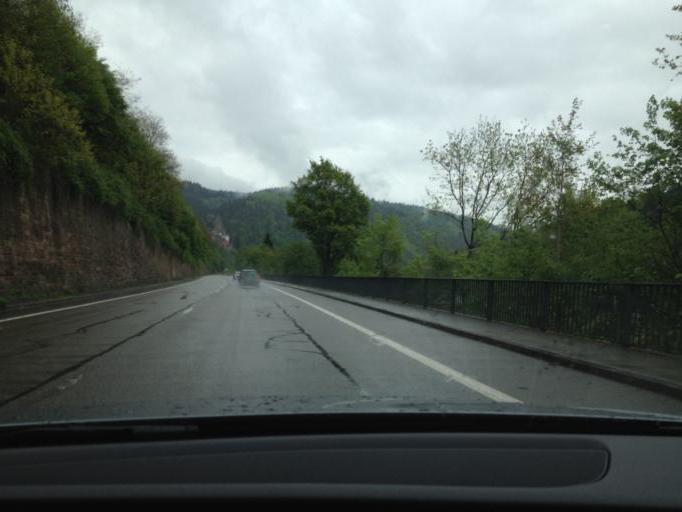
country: DE
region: Baden-Wuerttemberg
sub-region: Karlsruhe Region
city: Zwingenberg
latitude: 49.4165
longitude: 9.0178
